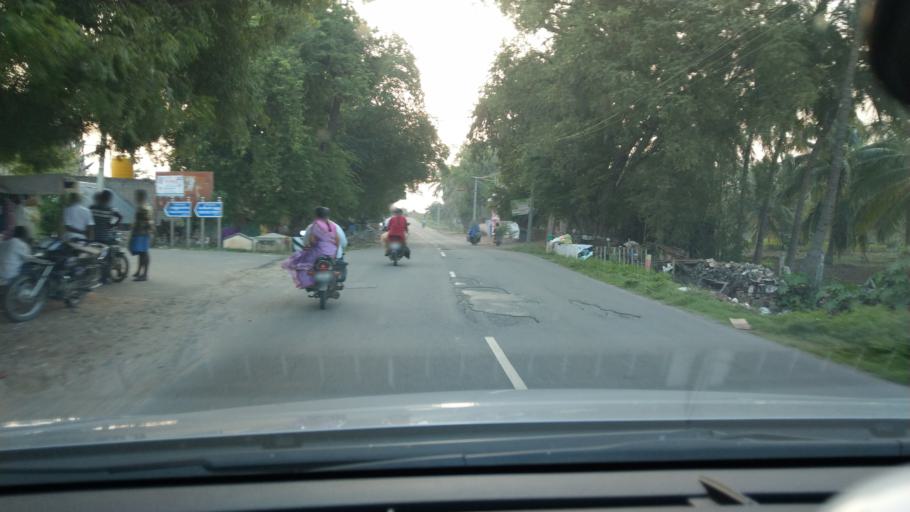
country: IN
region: Tamil Nadu
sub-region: Salem
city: Attur
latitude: 11.5990
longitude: 78.5773
